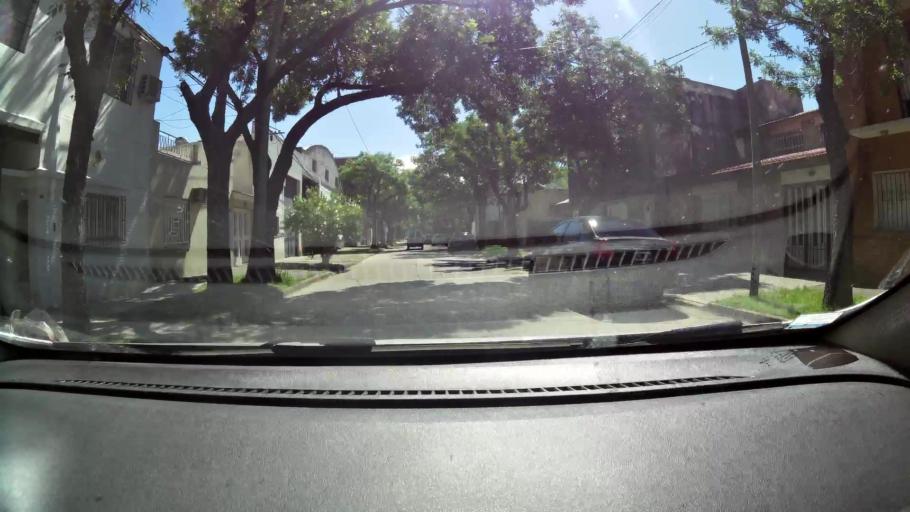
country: AR
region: Santa Fe
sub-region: Departamento de Rosario
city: Rosario
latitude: -32.9386
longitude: -60.6963
